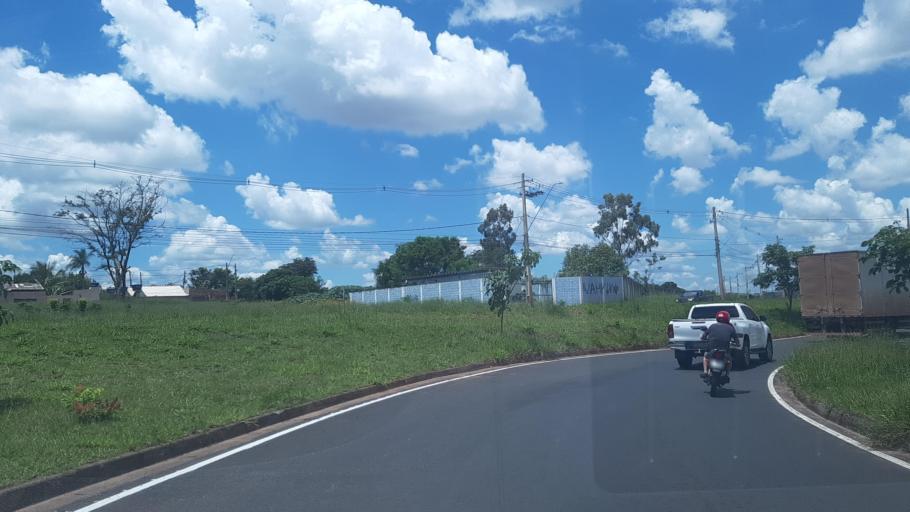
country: BR
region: Minas Gerais
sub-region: Uberlandia
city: Uberlandia
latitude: -18.9650
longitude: -48.3437
